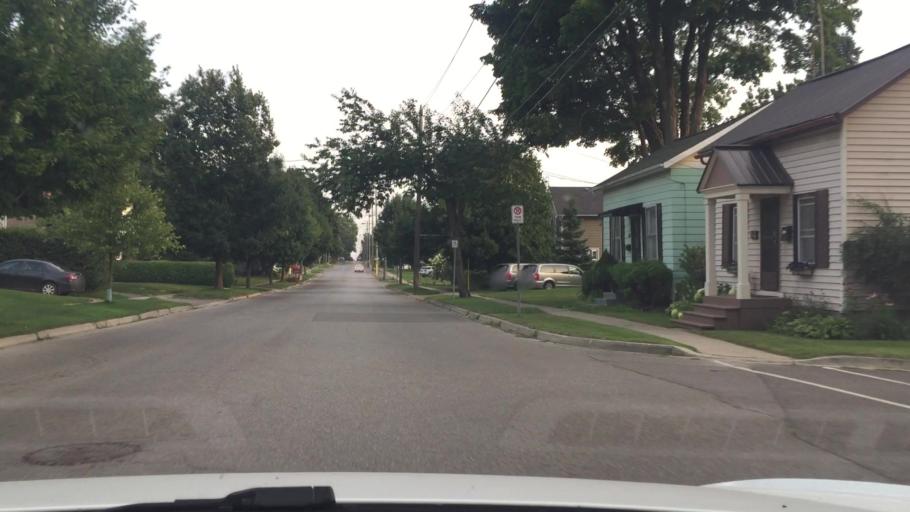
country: CA
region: Ontario
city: Cobourg
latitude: 43.9577
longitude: -78.2895
